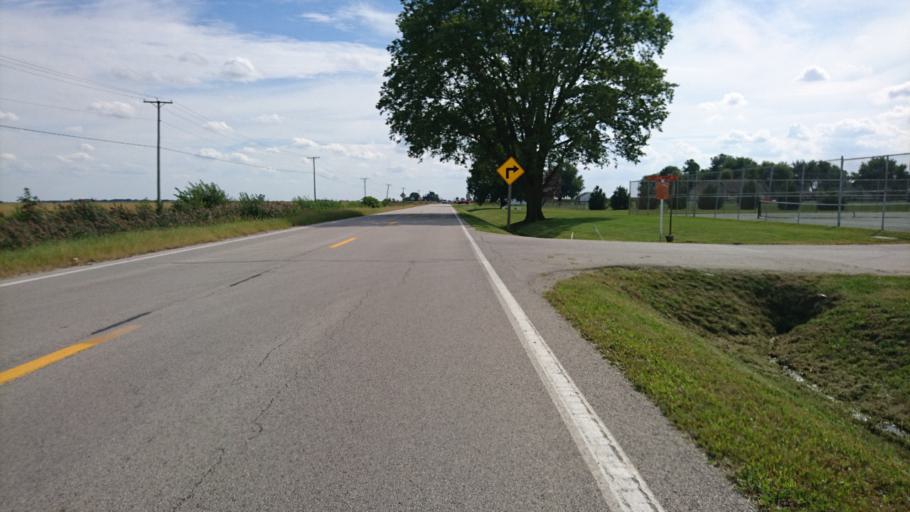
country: US
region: Illinois
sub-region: Grundy County
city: Gardner
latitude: 41.1855
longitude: -88.3011
